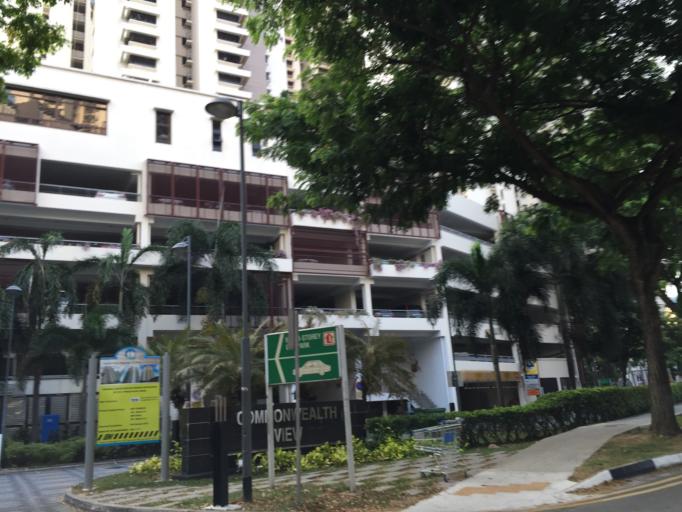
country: SG
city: Singapore
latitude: 1.3013
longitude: 103.7981
